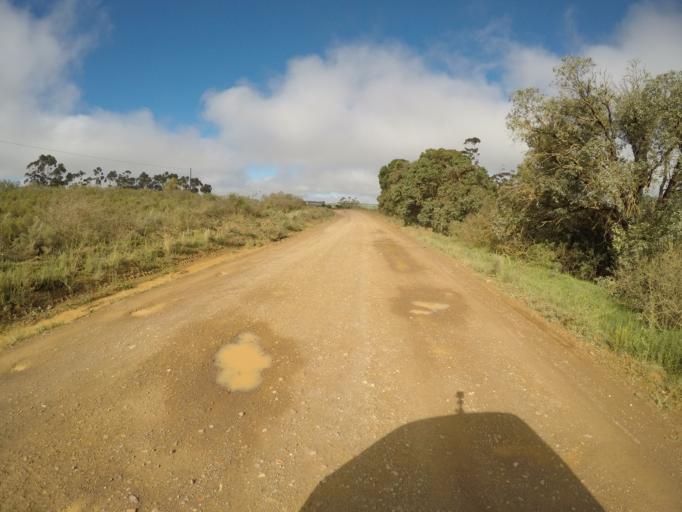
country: ZA
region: Western Cape
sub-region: Cape Winelands District Municipality
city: Ashton
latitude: -34.1210
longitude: 19.8071
